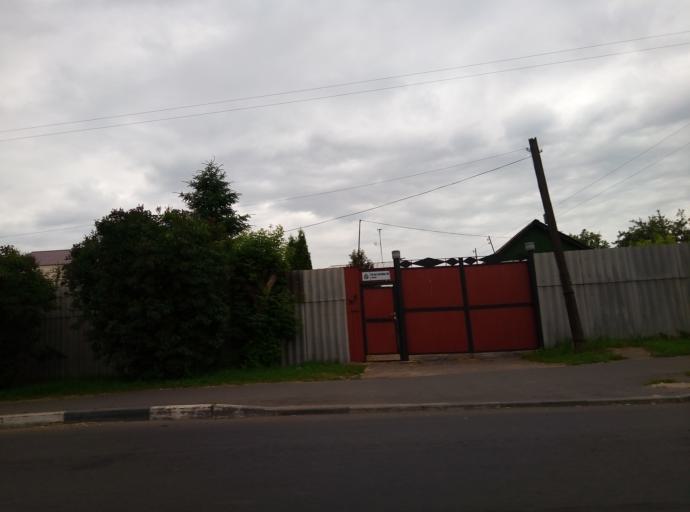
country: RU
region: Kursk
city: Kursk
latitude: 51.7320
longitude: 36.1553
